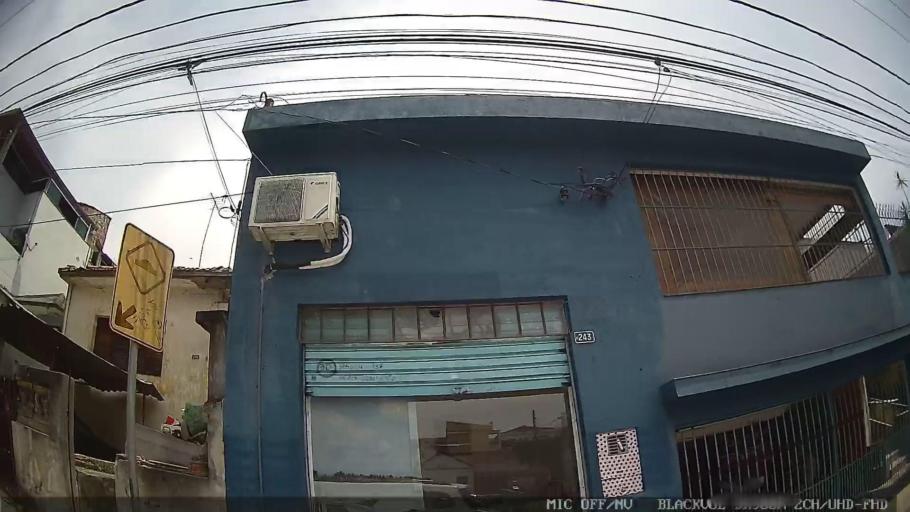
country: BR
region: Sao Paulo
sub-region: Sao Caetano Do Sul
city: Sao Caetano do Sul
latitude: -23.5687
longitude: -46.5600
